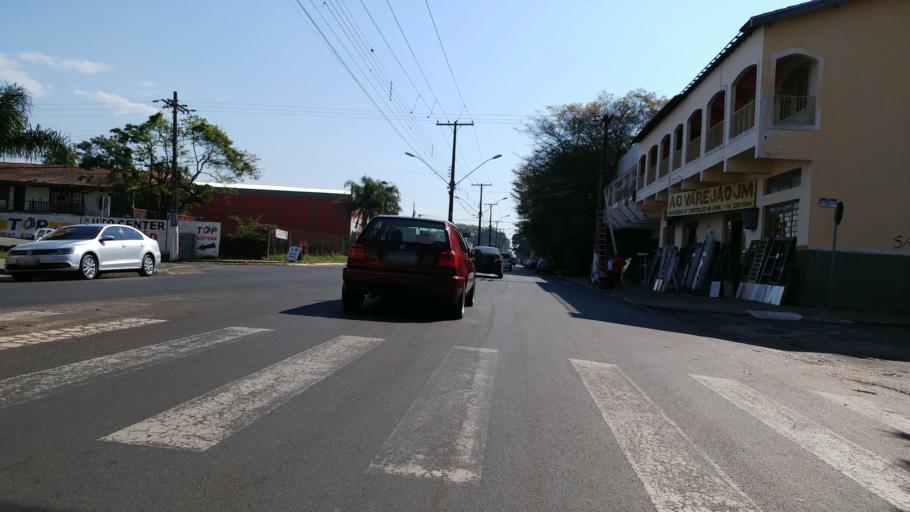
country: BR
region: Sao Paulo
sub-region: Paraguacu Paulista
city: Paraguacu Paulista
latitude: -22.4242
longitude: -50.5822
